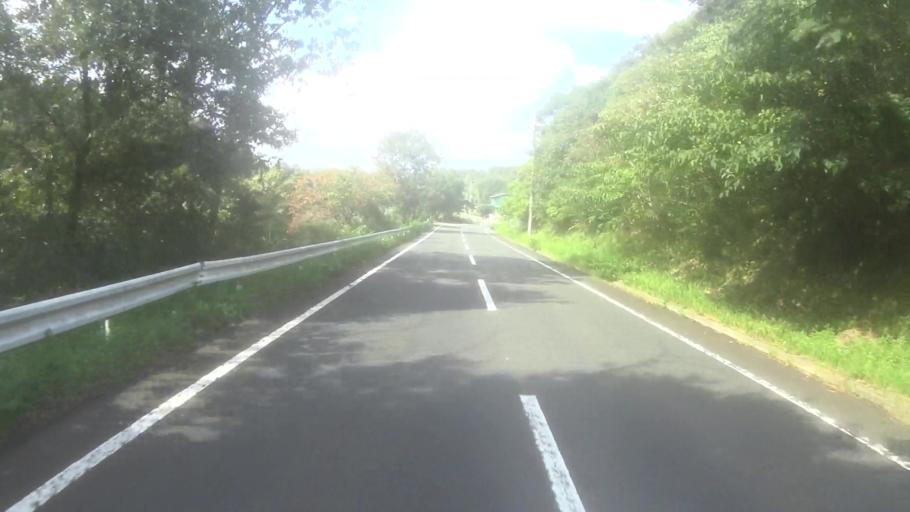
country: JP
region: Kyoto
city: Miyazu
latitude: 35.5872
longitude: 135.1146
